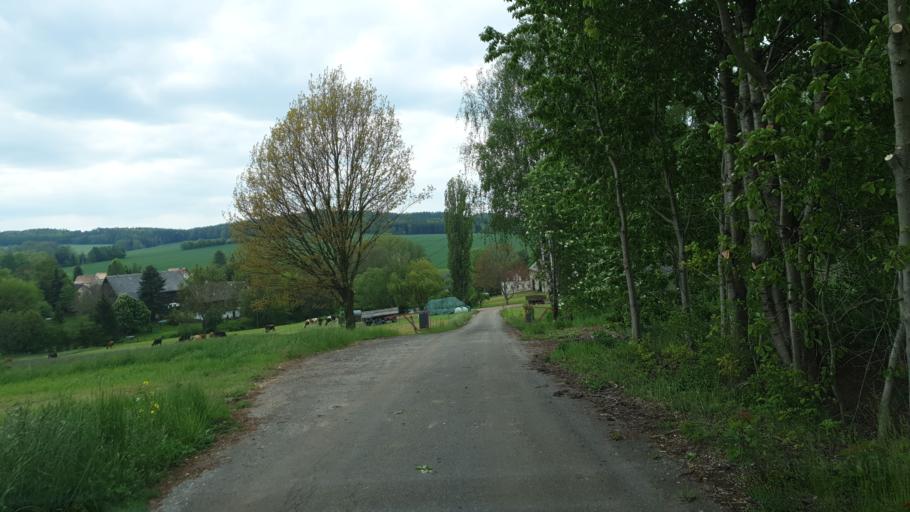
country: DE
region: Saxony
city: Bernsdorf
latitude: 50.7637
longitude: 12.6720
